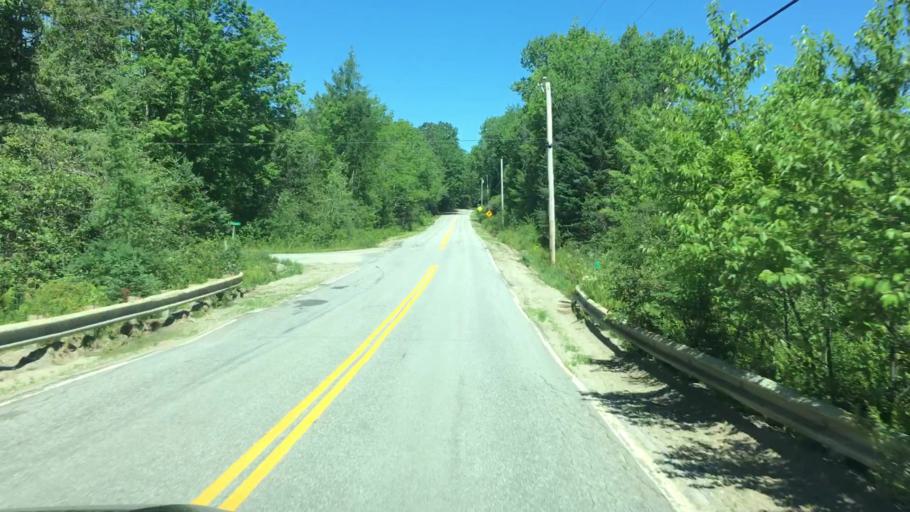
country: US
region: Maine
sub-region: Hancock County
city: Penobscot
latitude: 44.4258
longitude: -68.7101
